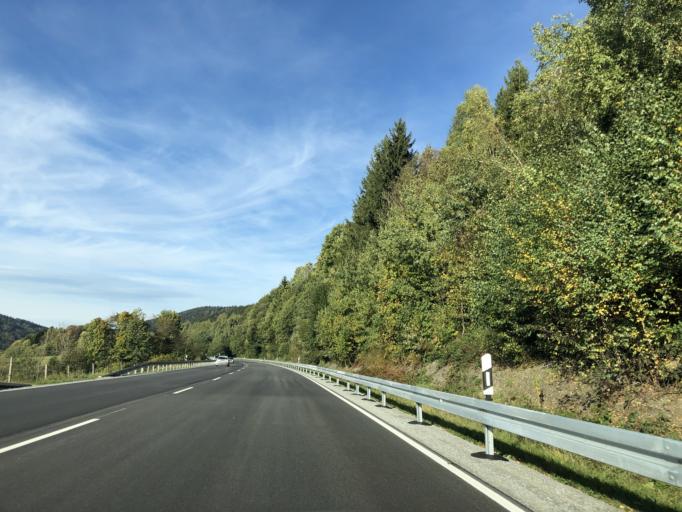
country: DE
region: Bavaria
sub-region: Lower Bavaria
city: Grafling
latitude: 48.9136
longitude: 12.9799
